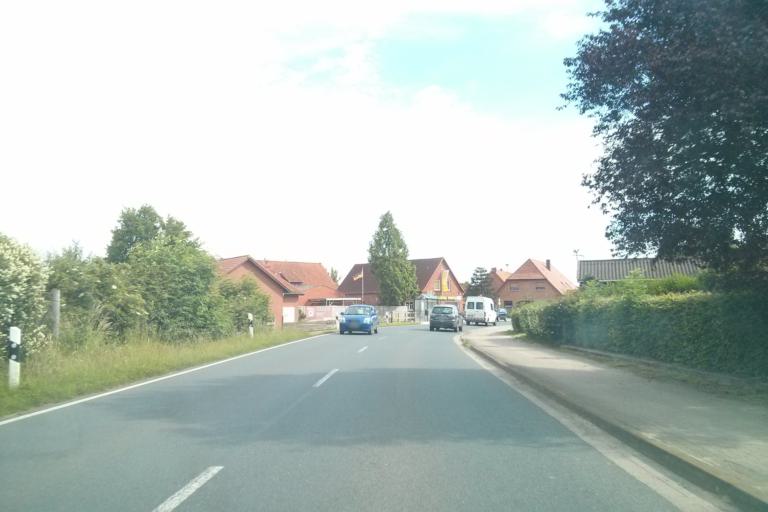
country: DE
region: Lower Saxony
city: Ahsen-Oetzen
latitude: 52.9686
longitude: 9.0490
